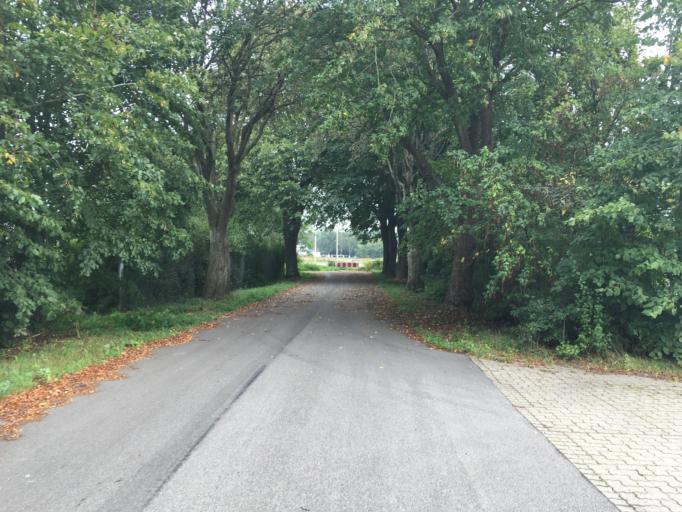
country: DK
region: Zealand
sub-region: Roskilde Kommune
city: Roskilde
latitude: 55.6236
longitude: 12.0569
